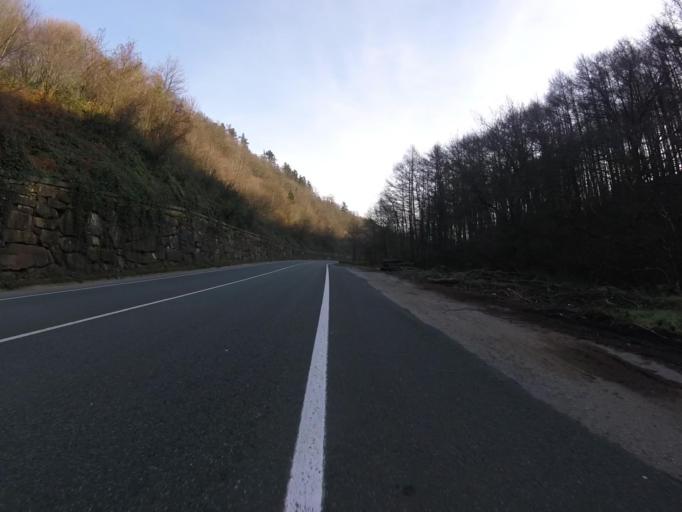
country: ES
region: Navarre
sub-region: Provincia de Navarra
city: Leitza
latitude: 43.0902
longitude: -1.9339
